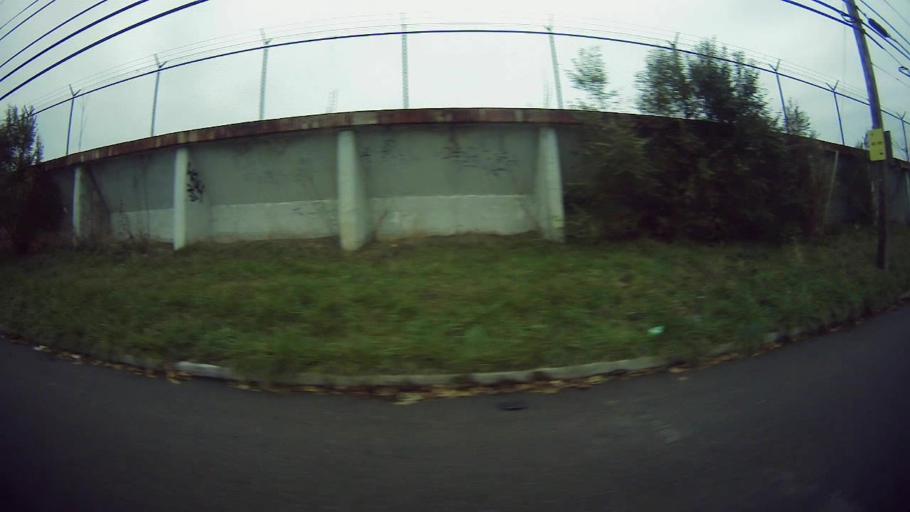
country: US
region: Michigan
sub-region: Wayne County
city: Highland Park
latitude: 42.4134
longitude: -83.0800
